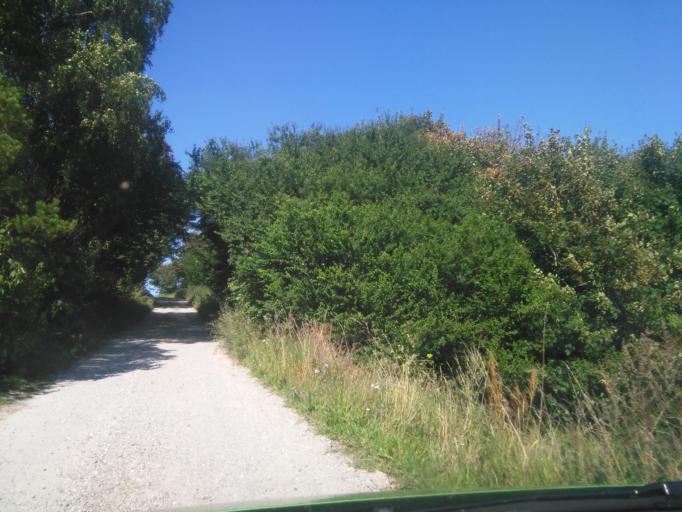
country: DK
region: Central Jutland
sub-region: Syddjurs Kommune
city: Ronde
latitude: 56.1966
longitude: 10.5372
